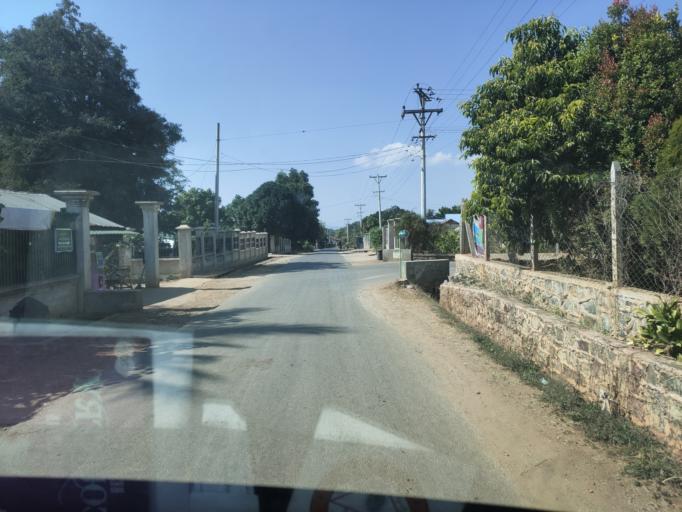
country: MM
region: Mandalay
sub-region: Pyin Oo Lwin District
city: Pyin Oo Lwin
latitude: 21.9534
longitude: 96.3929
